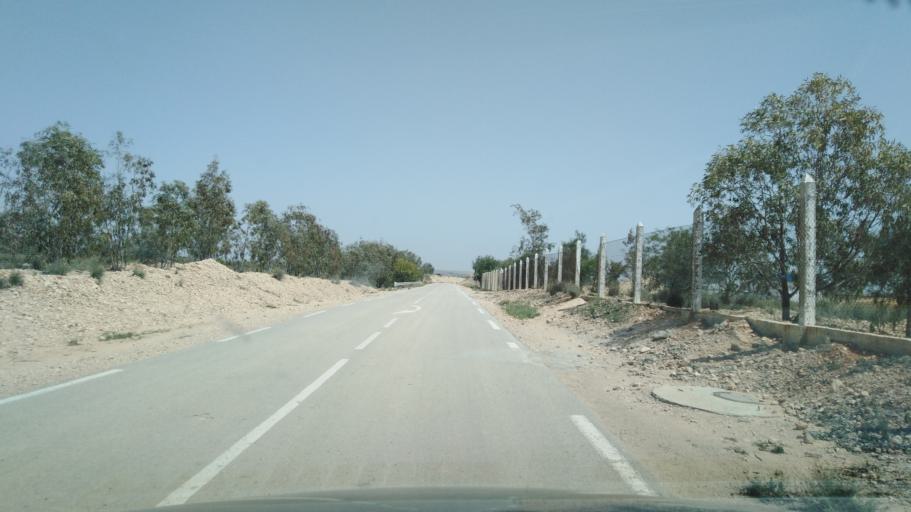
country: TN
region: Safaqis
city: Sfax
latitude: 34.7081
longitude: 10.5225
